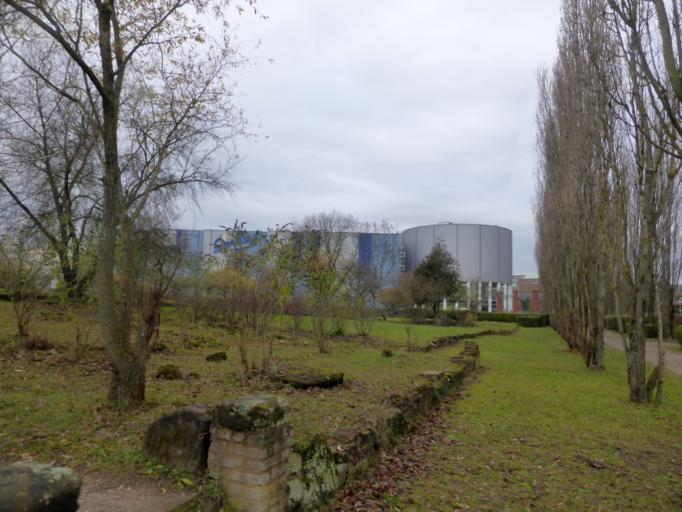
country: DE
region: Saarland
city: Saarbrucken
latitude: 49.2377
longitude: 6.9821
